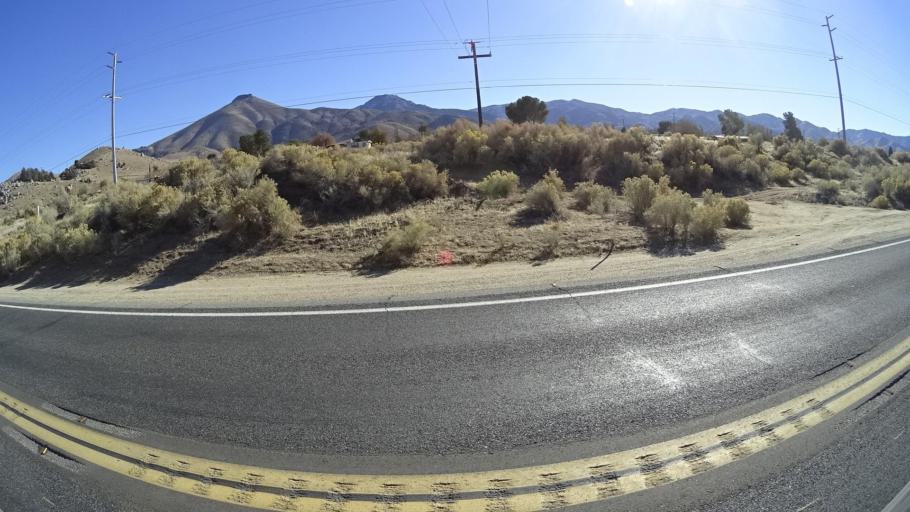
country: US
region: California
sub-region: Kern County
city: Weldon
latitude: 35.6573
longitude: -118.3237
